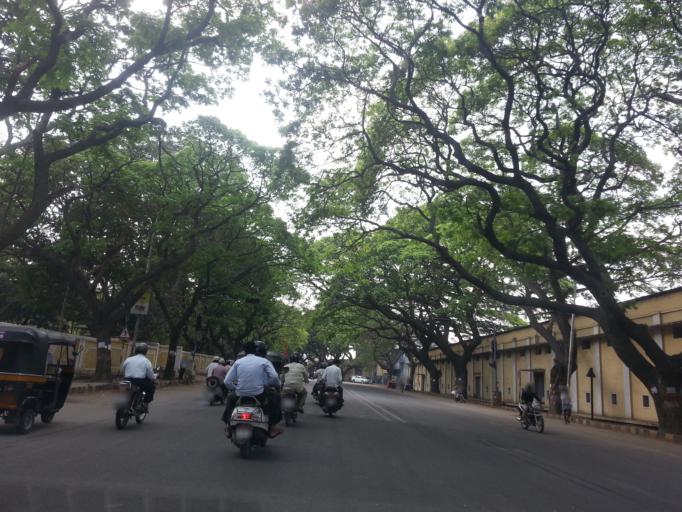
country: IN
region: Karnataka
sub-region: Mysore
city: Mysore
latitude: 12.3239
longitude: 76.6453
